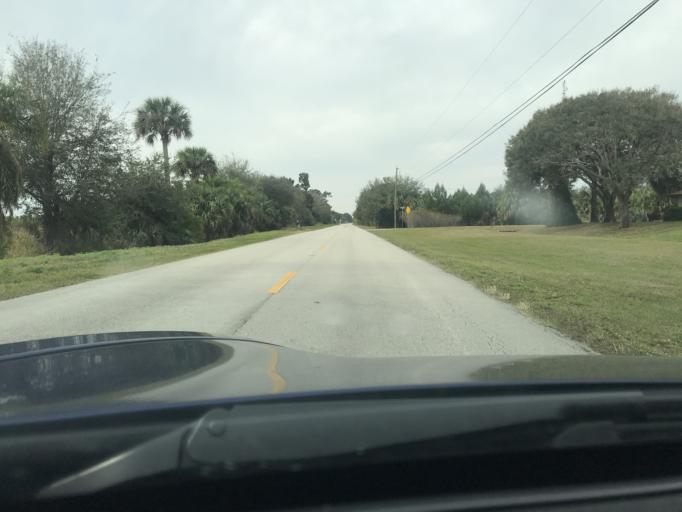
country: US
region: Florida
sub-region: Indian River County
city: Winter Beach
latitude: 27.7119
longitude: -80.4593
